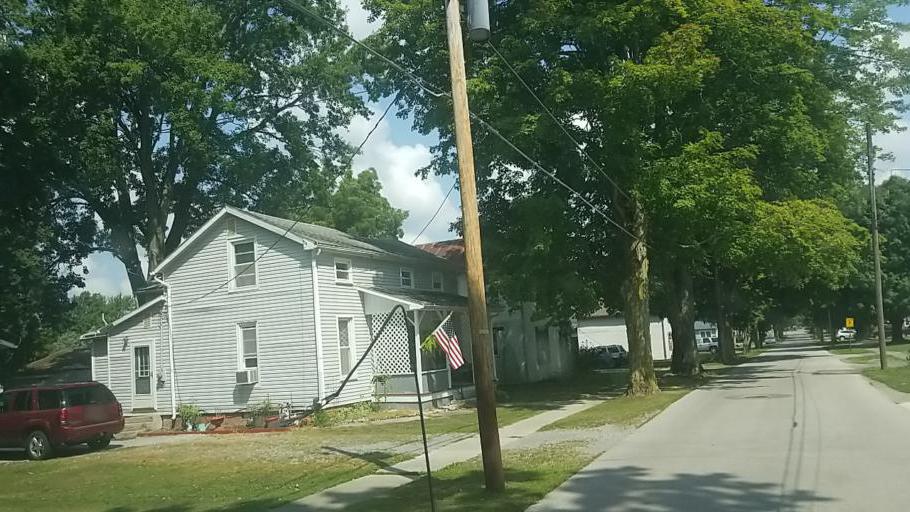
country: US
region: Ohio
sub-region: Wyandot County
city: Upper Sandusky
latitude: 40.8222
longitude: -83.2882
